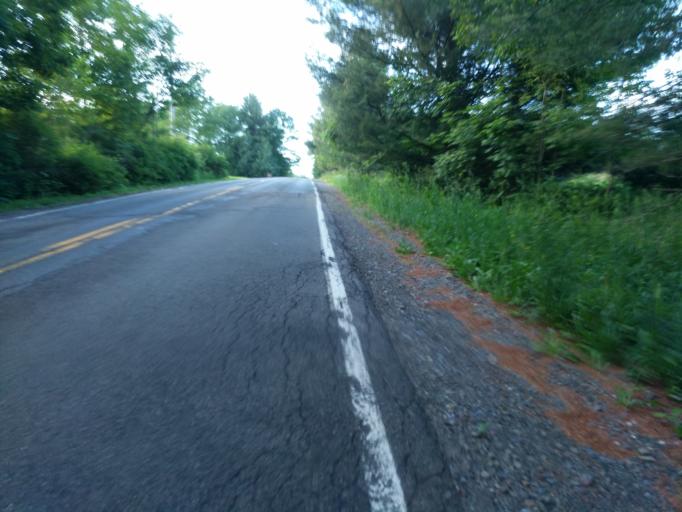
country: US
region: New York
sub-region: Tompkins County
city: Dryden
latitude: 42.4077
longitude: -76.3507
